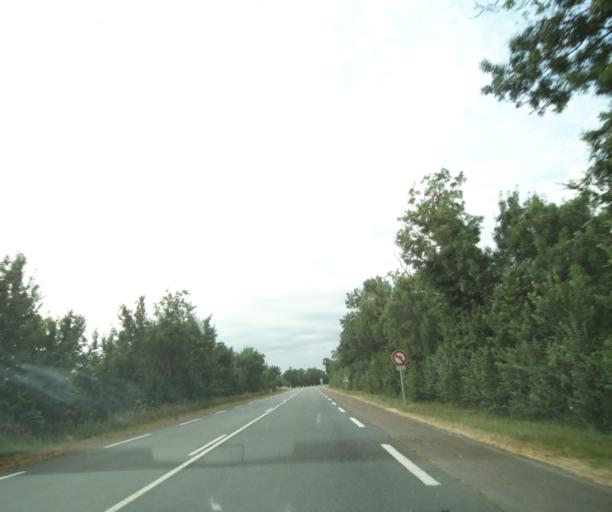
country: FR
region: Poitou-Charentes
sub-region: Departement de la Charente-Maritime
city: Marans
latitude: 46.3391
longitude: -0.9985
